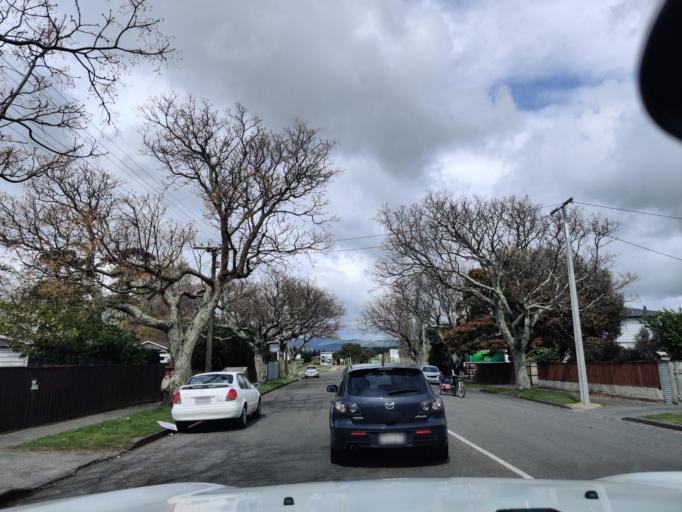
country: NZ
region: Manawatu-Wanganui
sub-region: Palmerston North City
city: Palmerston North
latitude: -40.3815
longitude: 175.5863
